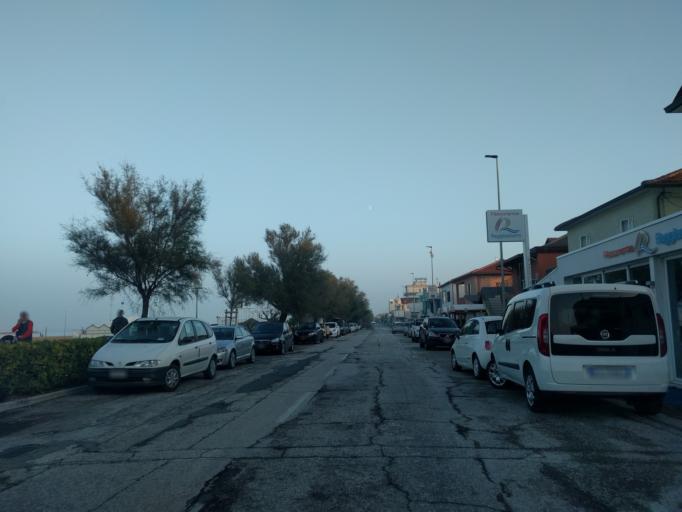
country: IT
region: The Marches
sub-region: Provincia di Ancona
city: Senigallia
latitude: 43.7283
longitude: 13.2041
